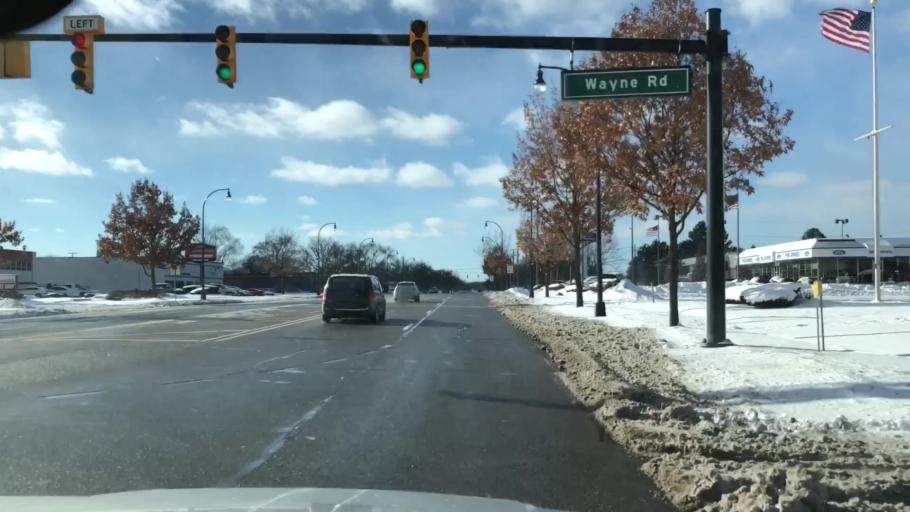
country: US
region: Michigan
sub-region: Wayne County
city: Livonia
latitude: 42.3681
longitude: -83.3869
